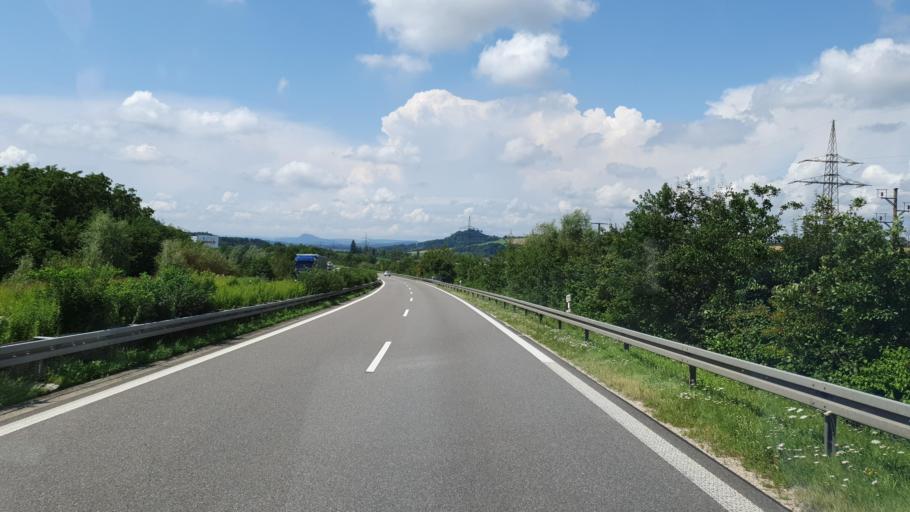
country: DE
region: Baden-Wuerttemberg
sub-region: Freiburg Region
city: Stockach
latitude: 47.8423
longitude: 9.0345
